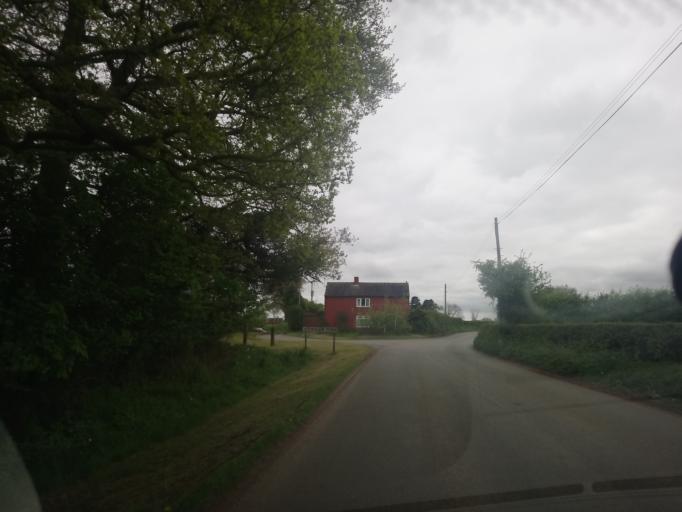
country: GB
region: England
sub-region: Shropshire
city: Stoke upon Tern
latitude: 52.8501
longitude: -2.5260
